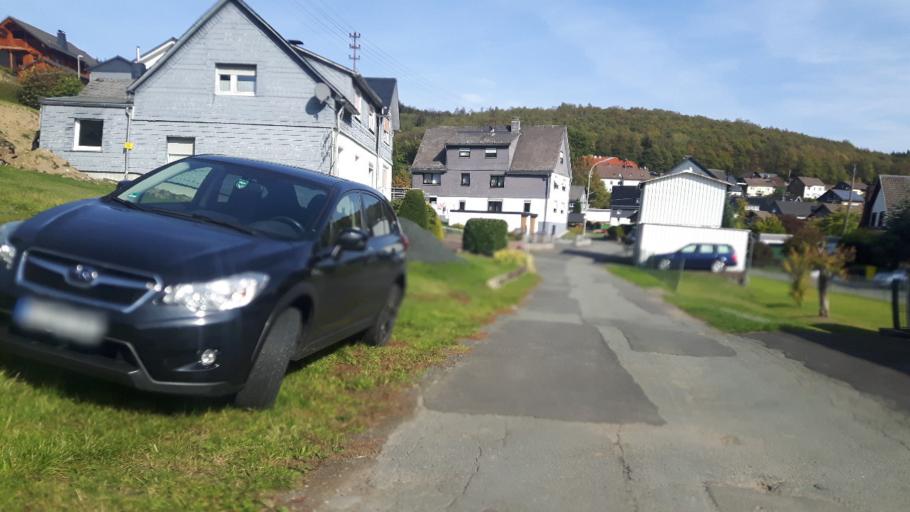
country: DE
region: North Rhine-Westphalia
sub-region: Regierungsbezirk Arnsberg
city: Erndtebruck
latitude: 50.9030
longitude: 8.2052
